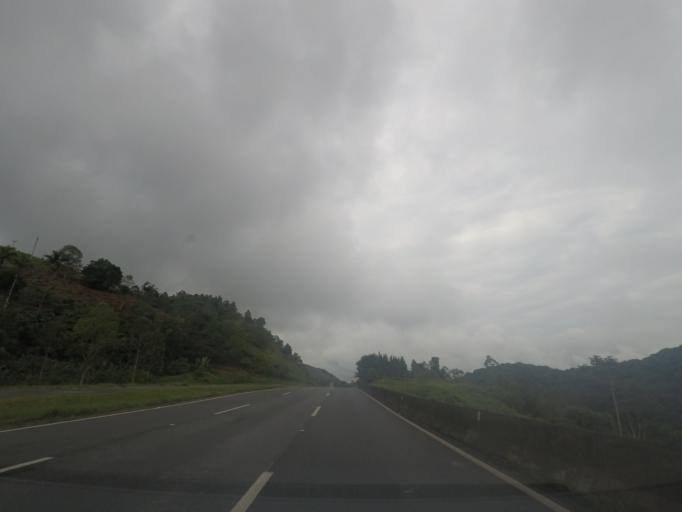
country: BR
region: Sao Paulo
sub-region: Cajati
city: Cajati
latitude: -24.9489
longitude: -48.4354
